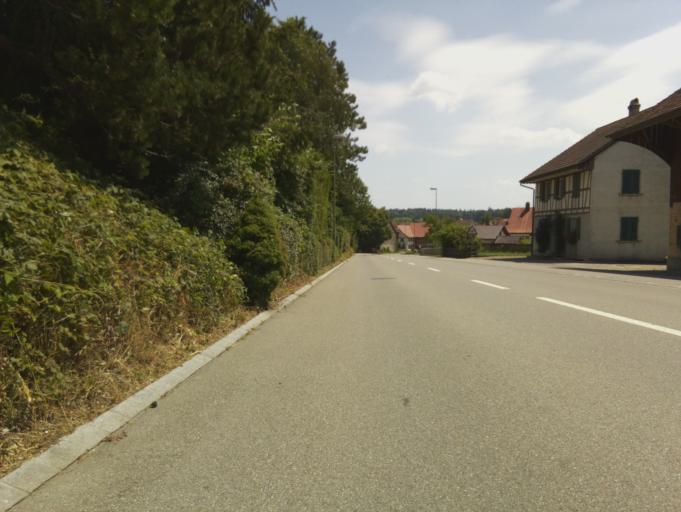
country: CH
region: Zurich
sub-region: Bezirk Andelfingen
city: Marthalen
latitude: 47.6258
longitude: 8.6730
